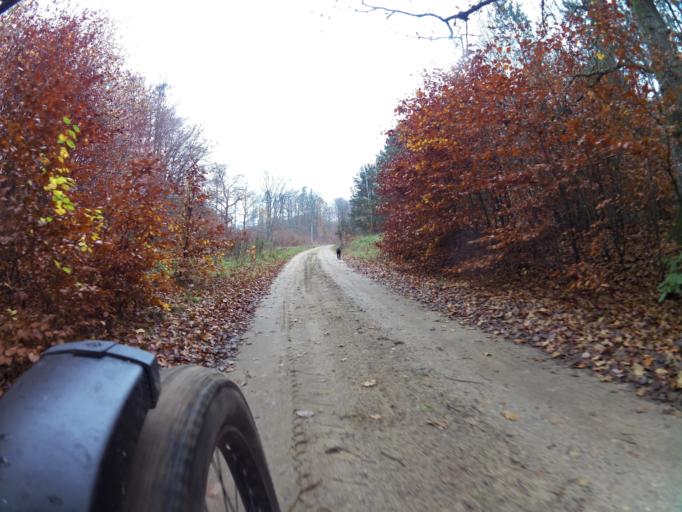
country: PL
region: Pomeranian Voivodeship
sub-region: Powiat pucki
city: Krokowa
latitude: 54.7148
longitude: 18.1403
